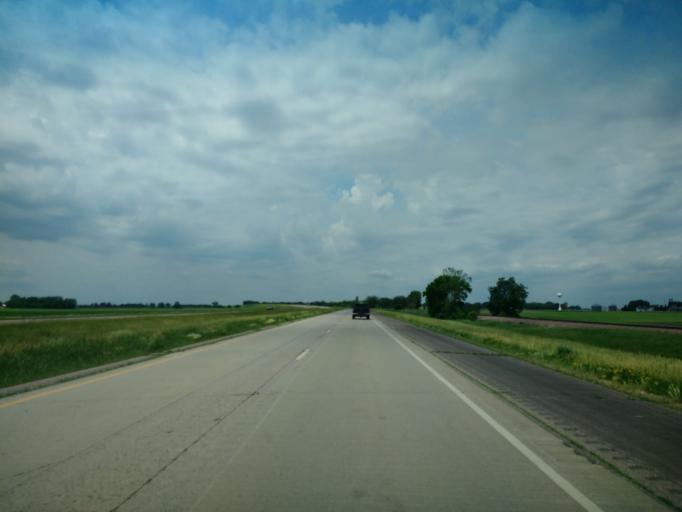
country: US
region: Minnesota
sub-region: Watonwan County
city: Saint James
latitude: 43.9612
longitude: -94.7676
